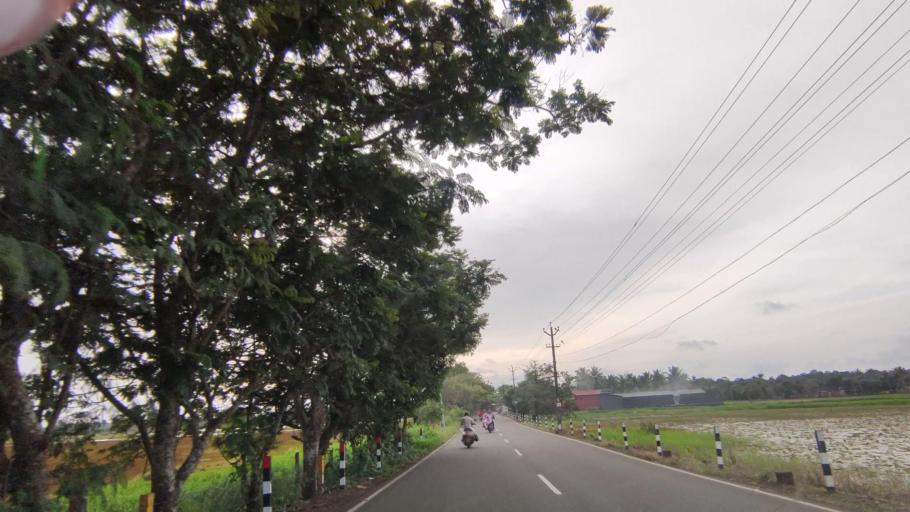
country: IN
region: Kerala
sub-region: Kottayam
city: Kottayam
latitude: 9.6917
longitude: 76.4938
